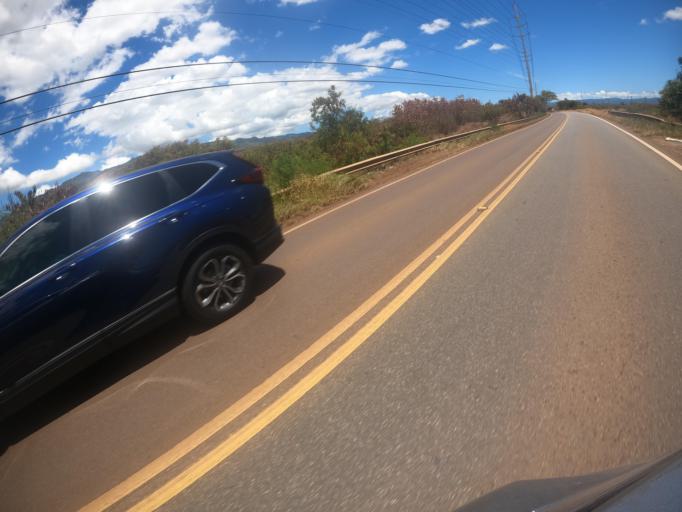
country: US
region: Hawaii
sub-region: Honolulu County
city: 'Ewa Villages
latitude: 21.3635
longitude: -158.0542
